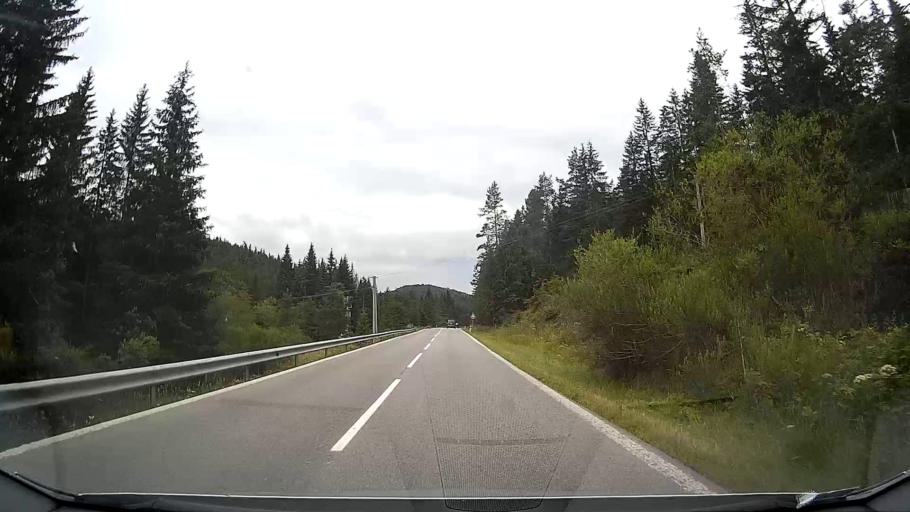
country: SK
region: Kosicky
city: Dobsina
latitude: 48.8818
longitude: 20.2341
